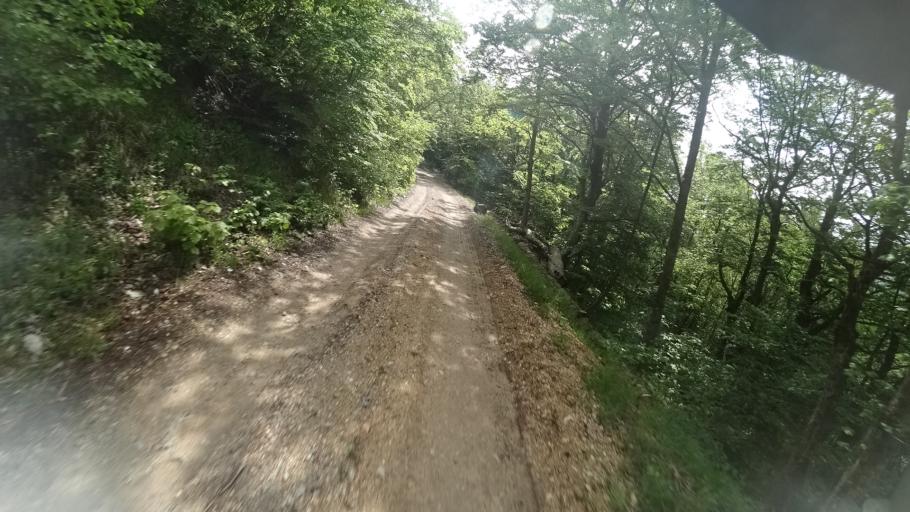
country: BA
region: Federation of Bosnia and Herzegovina
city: Bihac
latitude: 44.6829
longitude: 15.8373
